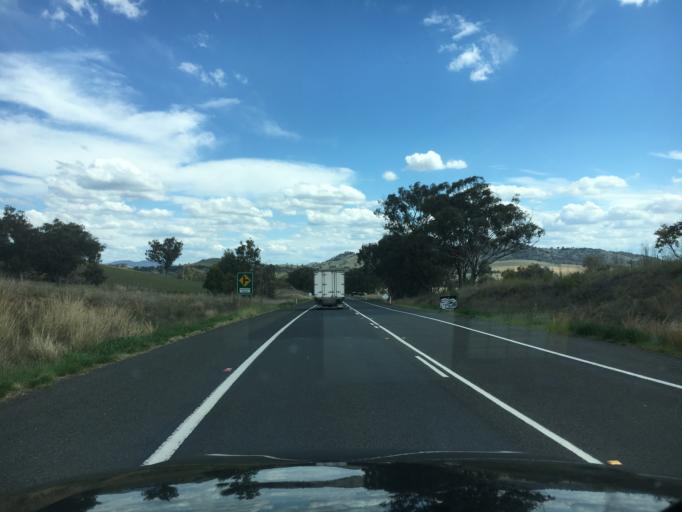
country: AU
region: New South Wales
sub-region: Liverpool Plains
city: Quirindi
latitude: -31.4661
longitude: 150.8610
